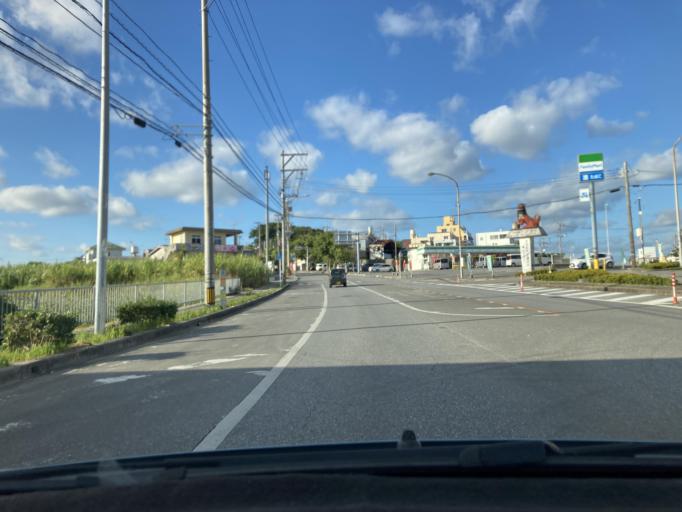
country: JP
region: Okinawa
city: Gushikawa
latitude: 26.3498
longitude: 127.8701
